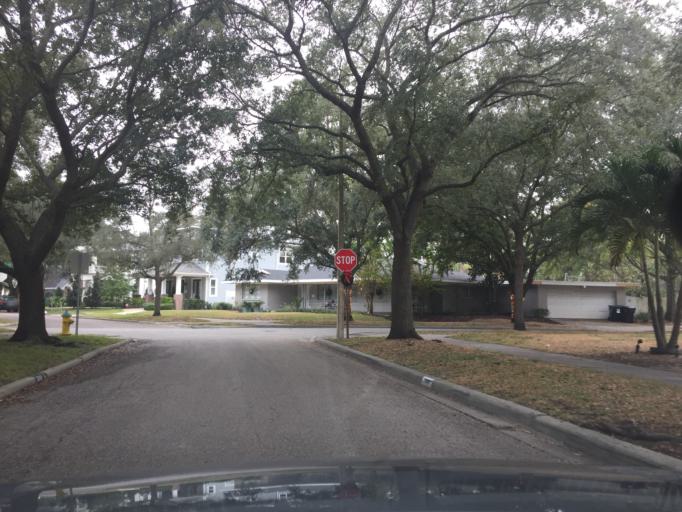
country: US
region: Florida
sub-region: Hillsborough County
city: Tampa
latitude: 27.9352
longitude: -82.4853
